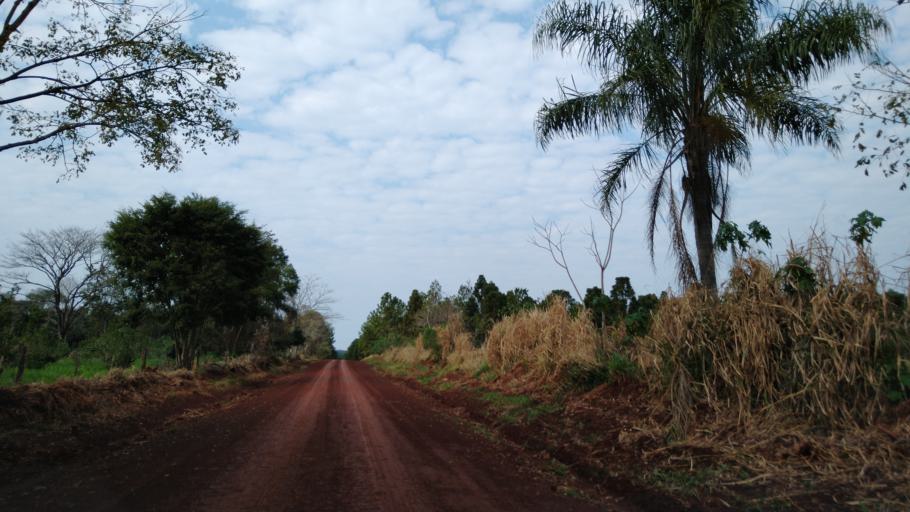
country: AR
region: Misiones
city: Capiovi
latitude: -26.9576
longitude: -55.0607
